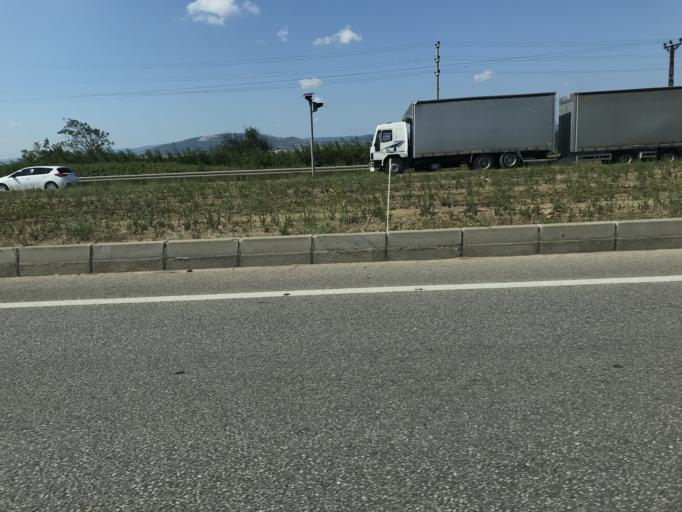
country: TR
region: Bursa
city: Karacabey
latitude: 40.1841
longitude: 28.3855
